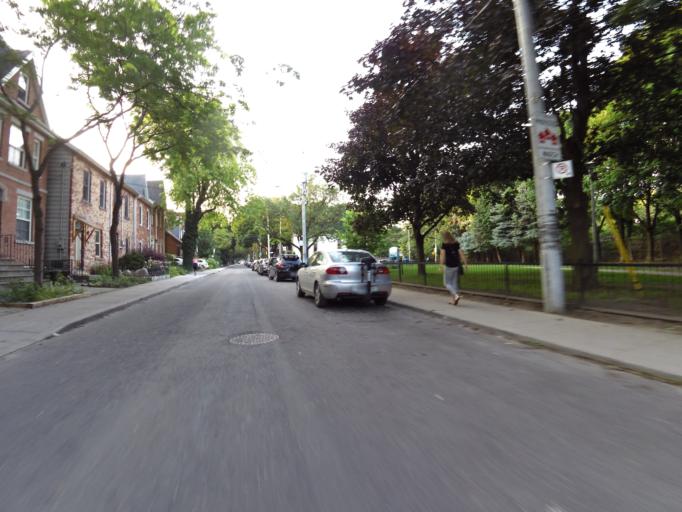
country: CA
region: Ontario
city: Toronto
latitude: 43.6606
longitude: -79.3462
